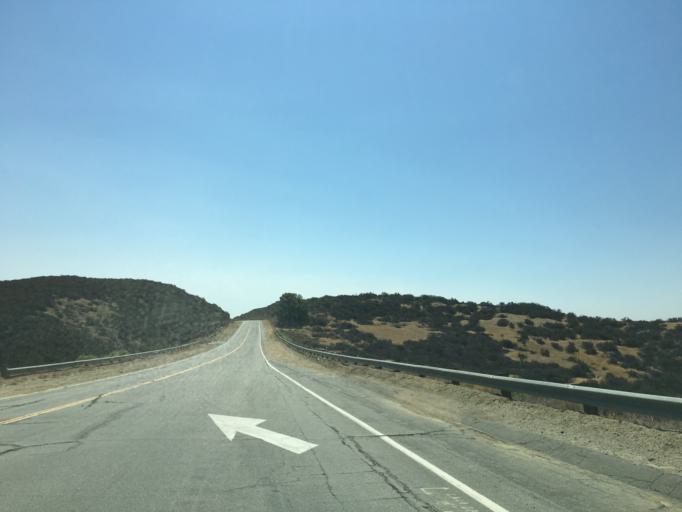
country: US
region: California
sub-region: Los Angeles County
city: Castaic
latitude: 34.5178
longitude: -118.5882
